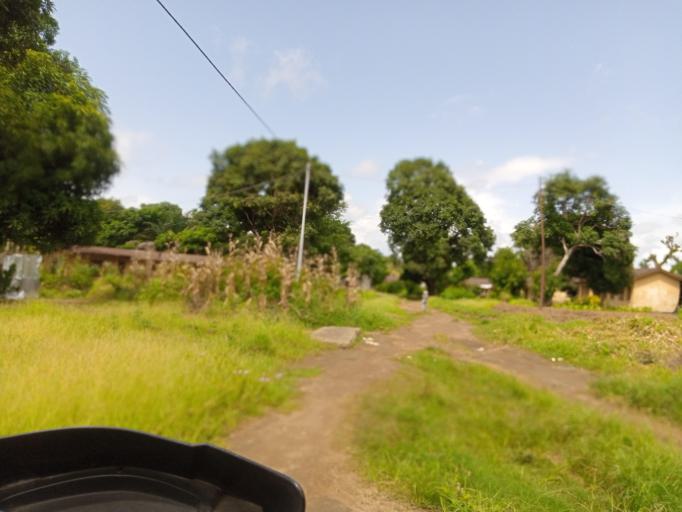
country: SL
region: Northern Province
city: Tintafor
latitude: 8.6247
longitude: -13.2108
